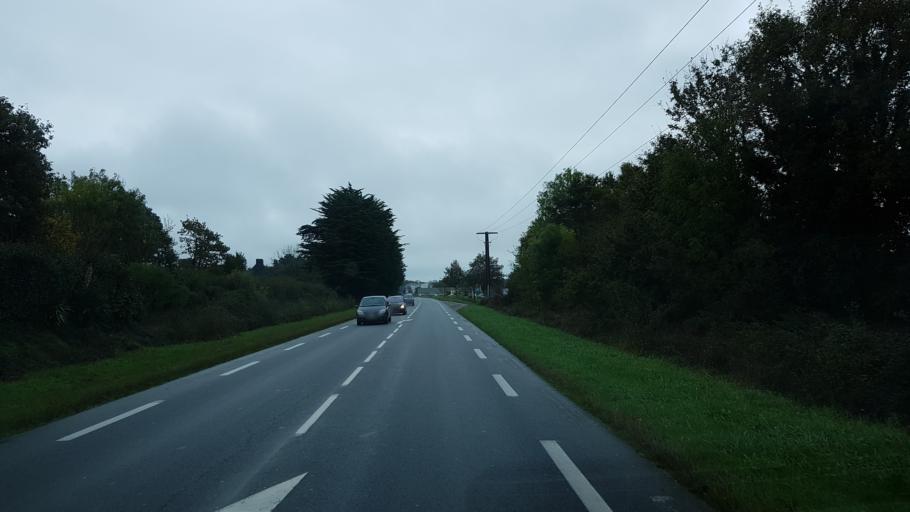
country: FR
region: Brittany
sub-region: Departement du Morbihan
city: Sarzeau
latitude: 47.5235
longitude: -2.7862
